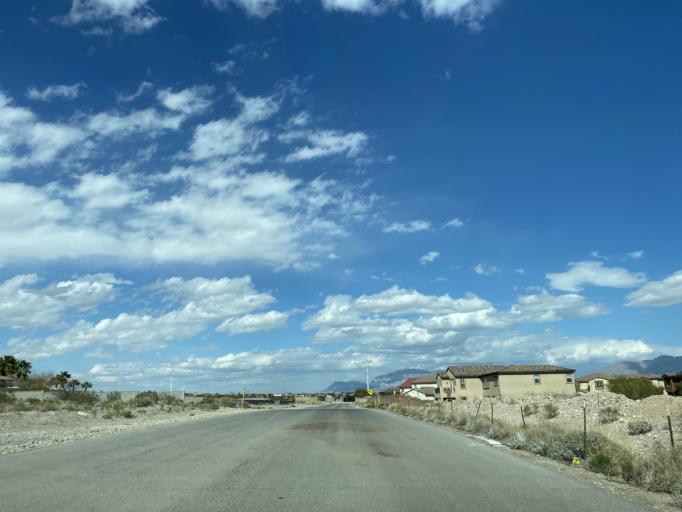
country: US
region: Nevada
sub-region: Clark County
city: Summerlin South
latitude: 36.2493
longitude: -115.3082
